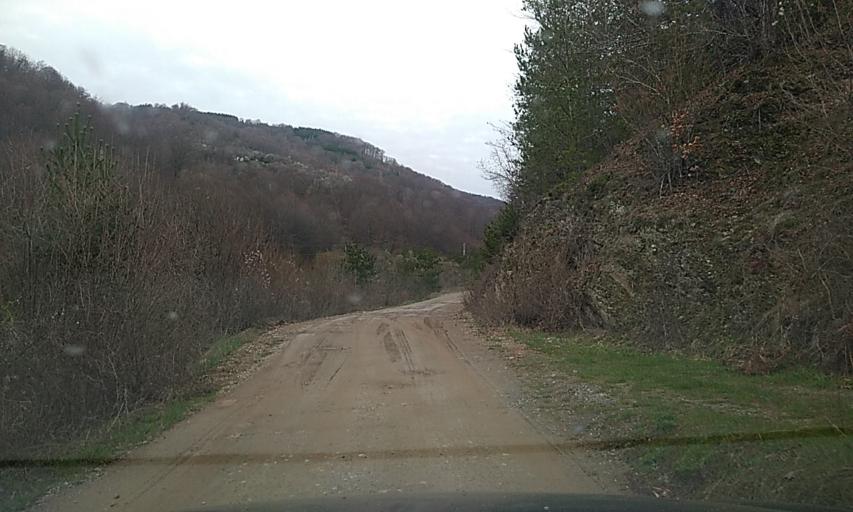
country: MK
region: Kriva Palanka
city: Kriva Palanka
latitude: 42.3405
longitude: 22.3874
